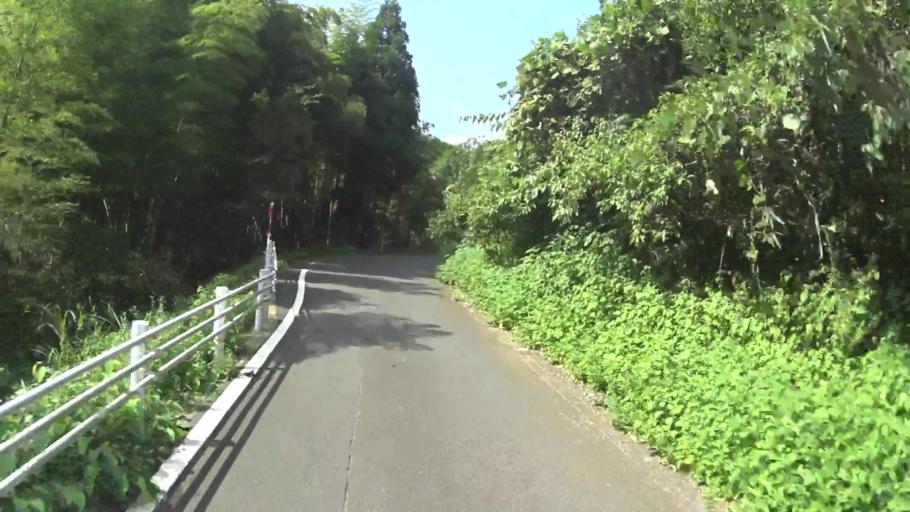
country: JP
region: Kyoto
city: Miyazu
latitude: 35.6557
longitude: 135.2531
